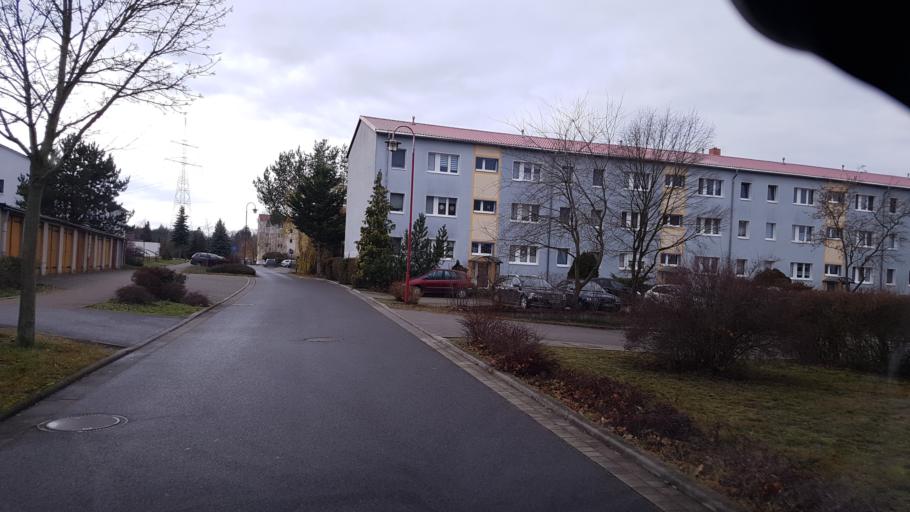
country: DE
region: Brandenburg
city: Altdobern
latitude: 51.6513
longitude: 14.0187
